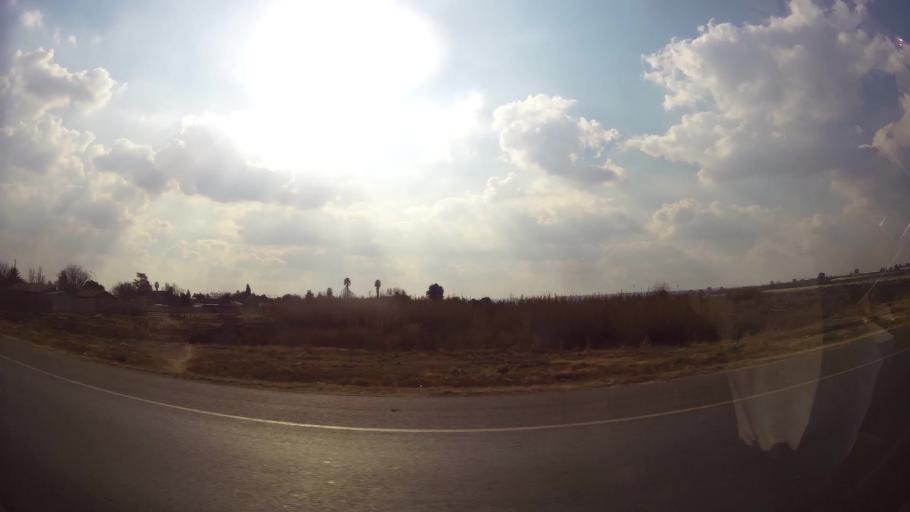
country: ZA
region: Gauteng
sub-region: Ekurhuleni Metropolitan Municipality
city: Germiston
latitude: -26.2931
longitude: 28.2173
